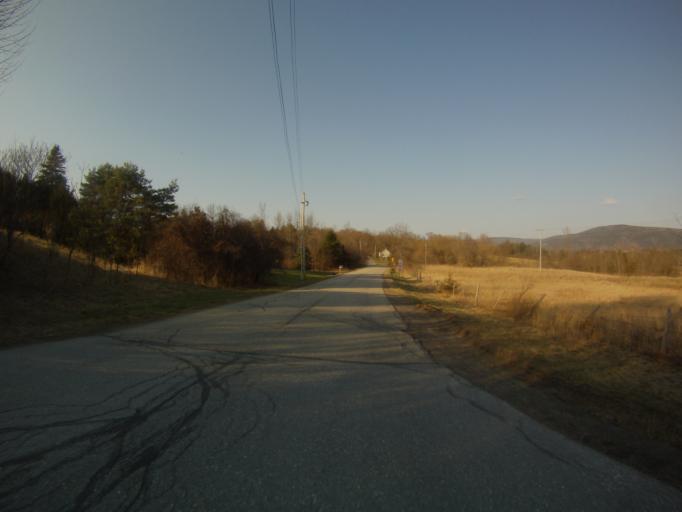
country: US
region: Vermont
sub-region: Addison County
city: Middlebury (village)
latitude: 44.0283
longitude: -73.1470
